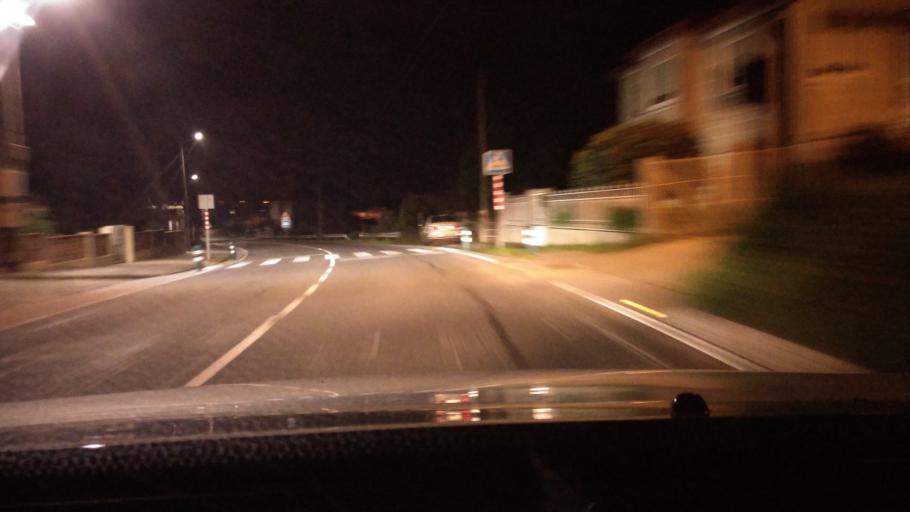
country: ES
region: Galicia
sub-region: Provincia de Pontevedra
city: Moana
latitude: 42.2761
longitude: -8.7491
